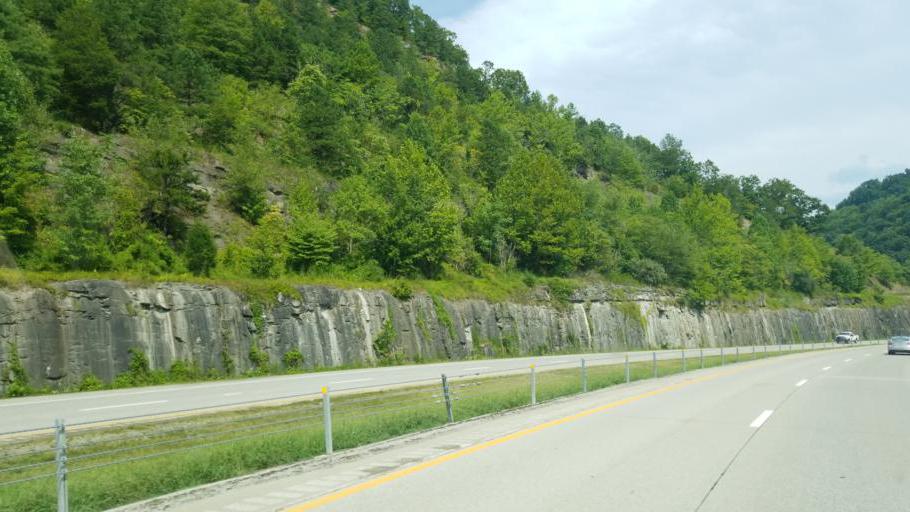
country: US
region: West Virginia
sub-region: Boone County
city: Madison
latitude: 38.1536
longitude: -81.8464
